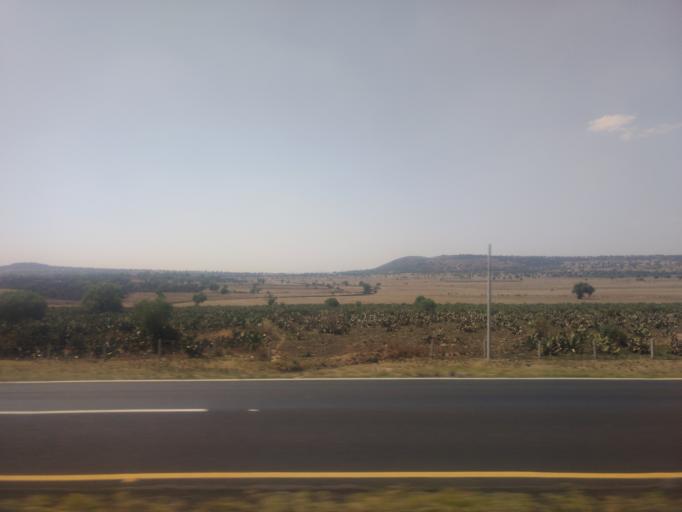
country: MX
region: Morelos
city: Nopaltepec
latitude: 19.8149
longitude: -98.7157
